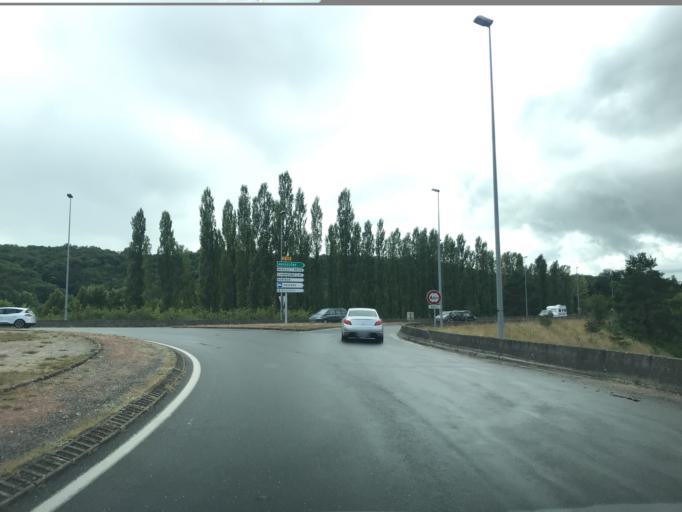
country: FR
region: Aquitaine
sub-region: Departement de la Dordogne
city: Brantome
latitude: 45.3541
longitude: 0.6531
